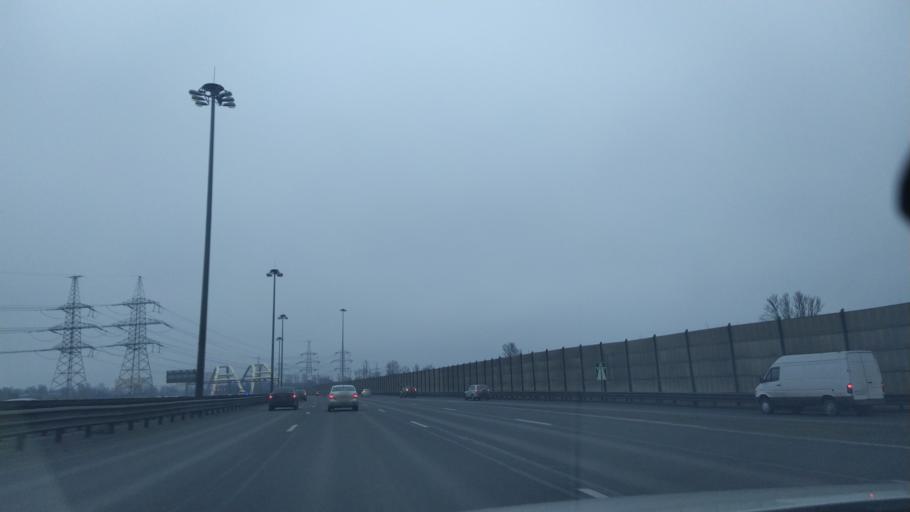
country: RU
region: St.-Petersburg
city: Krasnogvargeisky
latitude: 59.9889
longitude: 30.4851
